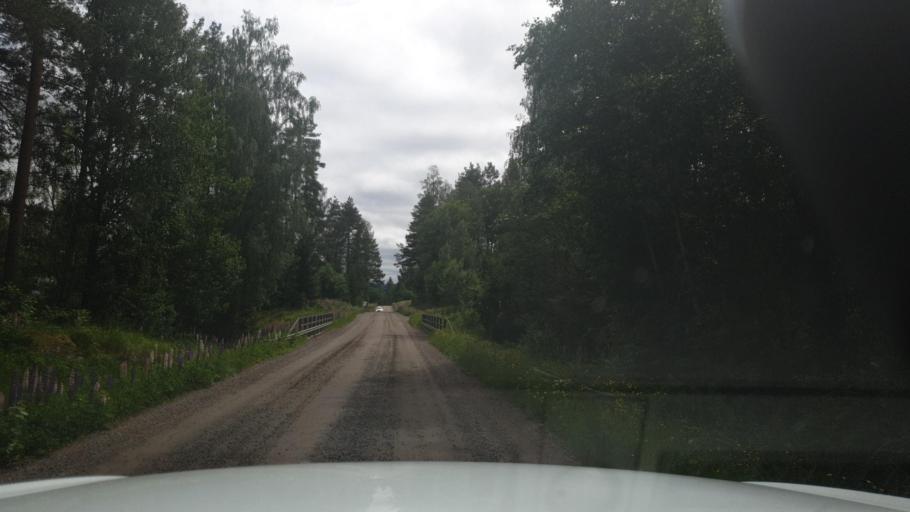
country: NO
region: Ostfold
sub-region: Romskog
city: Romskog
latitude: 59.8500
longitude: 11.9638
